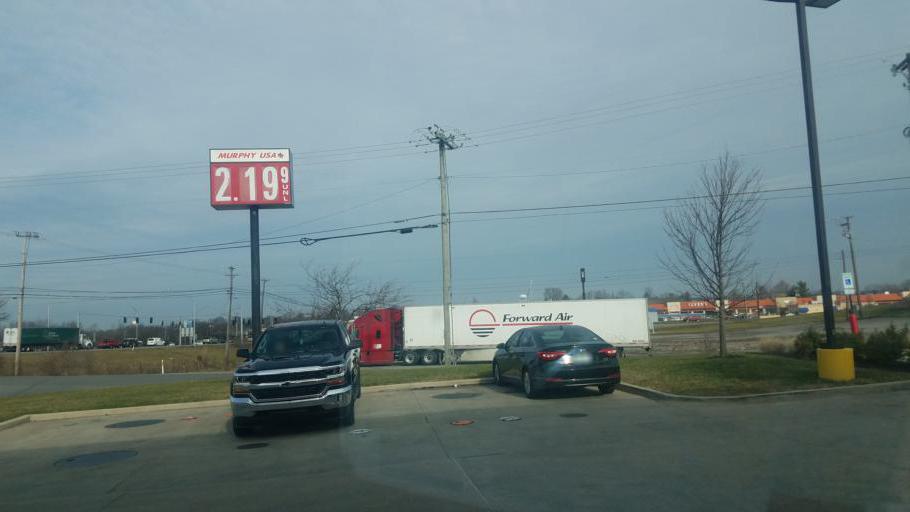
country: US
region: Kentucky
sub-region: Boyle County
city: Danville
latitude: 37.6161
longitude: -84.7735
